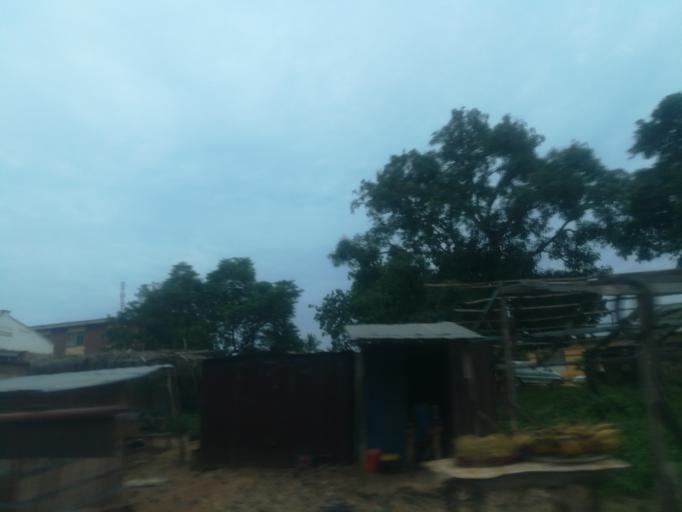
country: NG
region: Oyo
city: Moniya
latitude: 7.4582
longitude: 3.9093
